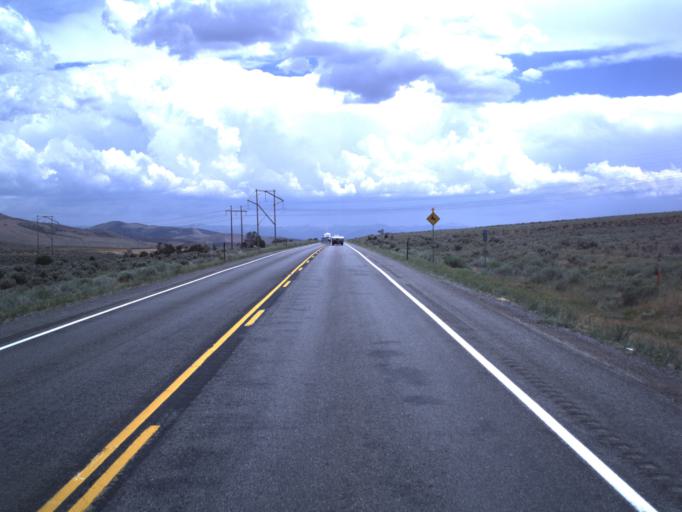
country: US
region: Utah
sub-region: Sanpete County
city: Fountain Green
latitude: 39.6939
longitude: -111.6901
